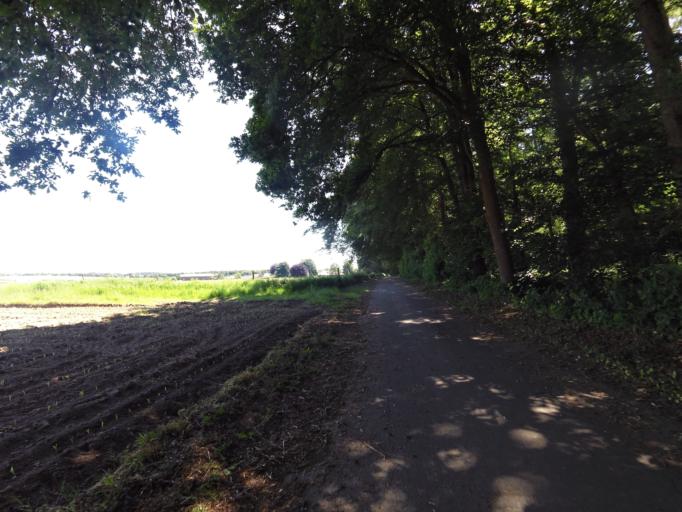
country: NL
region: Limburg
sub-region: Gemeente Onderbanken
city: Schinveld
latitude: 50.9855
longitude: 5.9727
